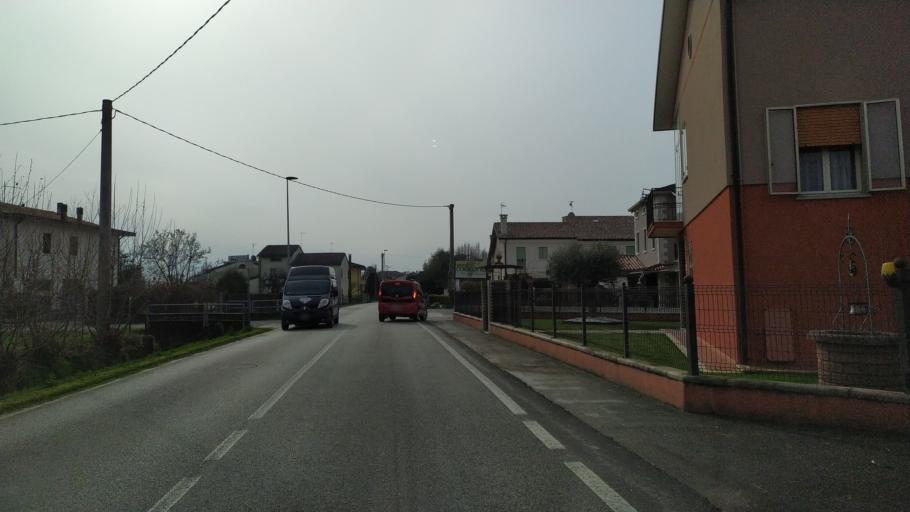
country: IT
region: Veneto
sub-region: Provincia di Padova
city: San Pietro in Gu
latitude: 45.6234
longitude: 11.6721
